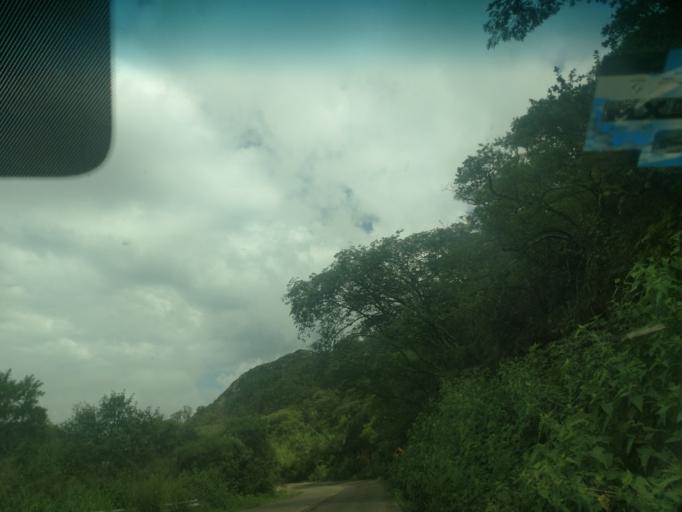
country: MX
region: Jalisco
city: El Salto
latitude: 20.3676
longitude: -104.5900
